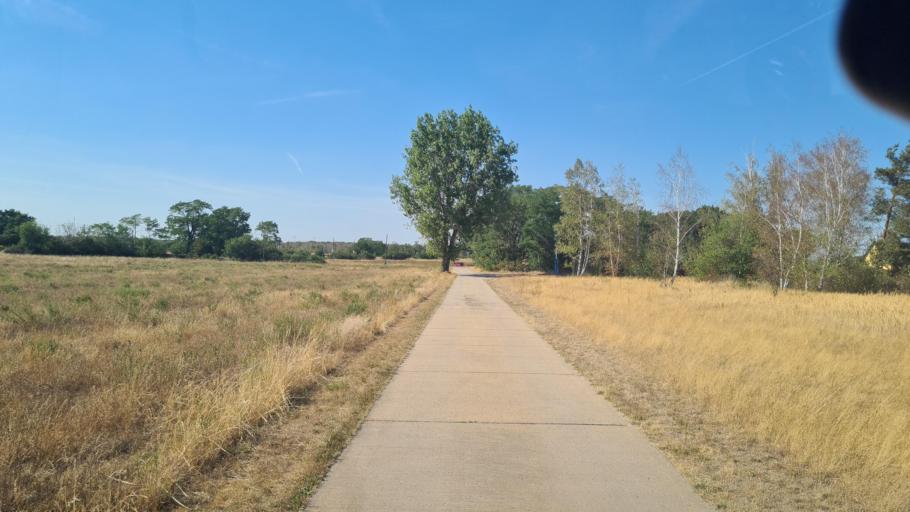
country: DE
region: Saxony
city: Zeithain
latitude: 51.3808
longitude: 13.3146
